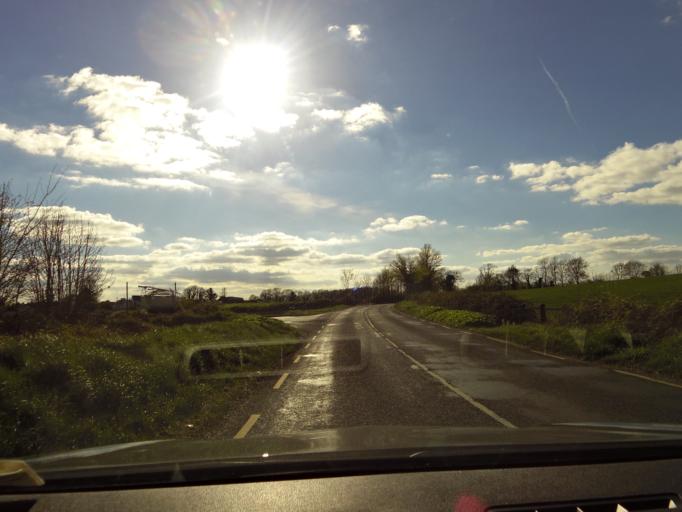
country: IE
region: Connaught
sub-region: County Galway
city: Portumna
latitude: 53.0983
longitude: -8.1672
